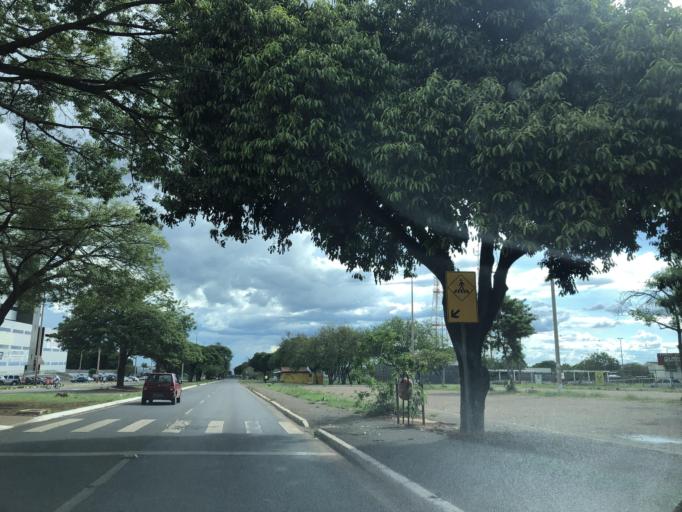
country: BR
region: Goias
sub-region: Luziania
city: Luziania
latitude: -16.0197
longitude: -48.0680
